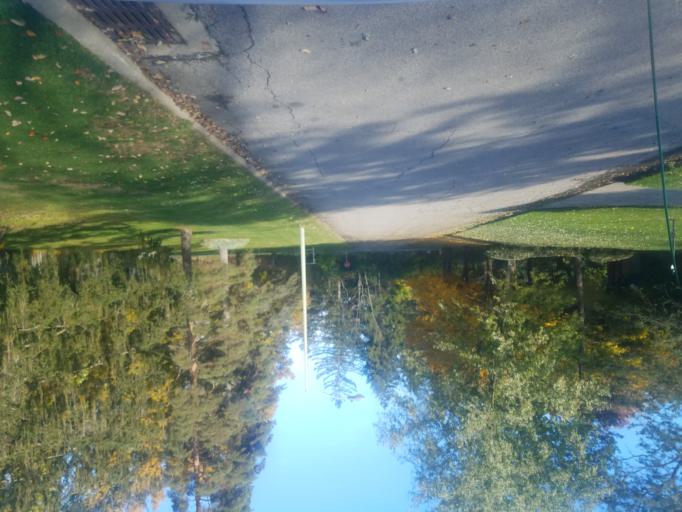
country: US
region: Ohio
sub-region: Richland County
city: Mansfield
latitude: 40.7368
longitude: -82.5412
